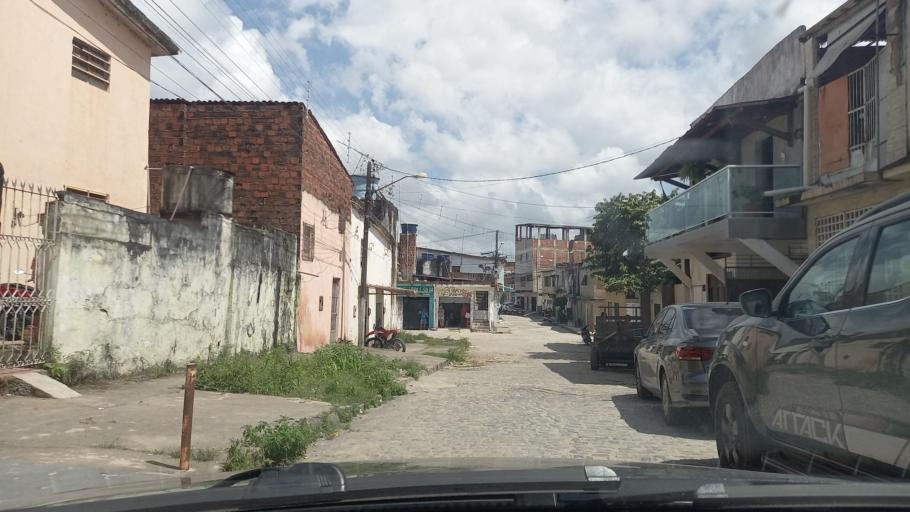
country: BR
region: Pernambuco
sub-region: Goiana
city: Goiana
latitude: -7.5621
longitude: -34.9920
